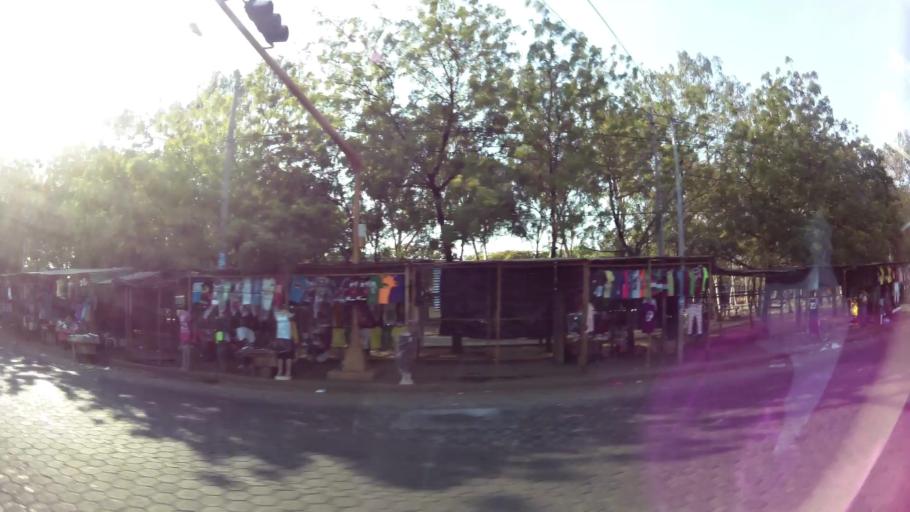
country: NI
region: Managua
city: Managua
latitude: 12.1441
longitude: -86.2619
